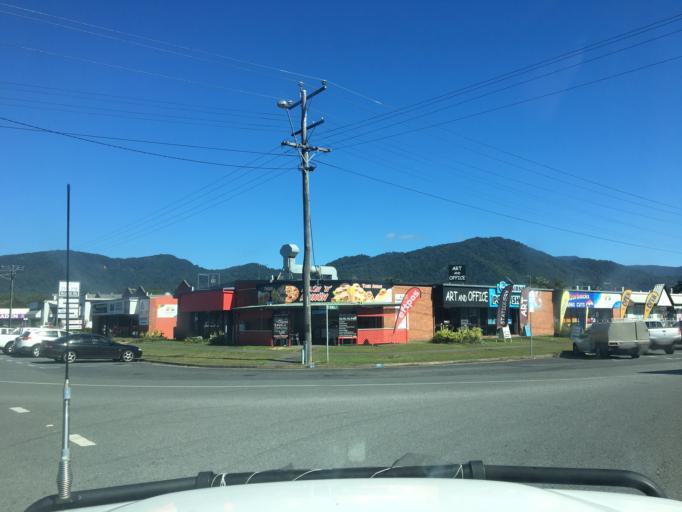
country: AU
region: Queensland
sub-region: Cairns
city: Woree
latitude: -16.9400
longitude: 145.7525
